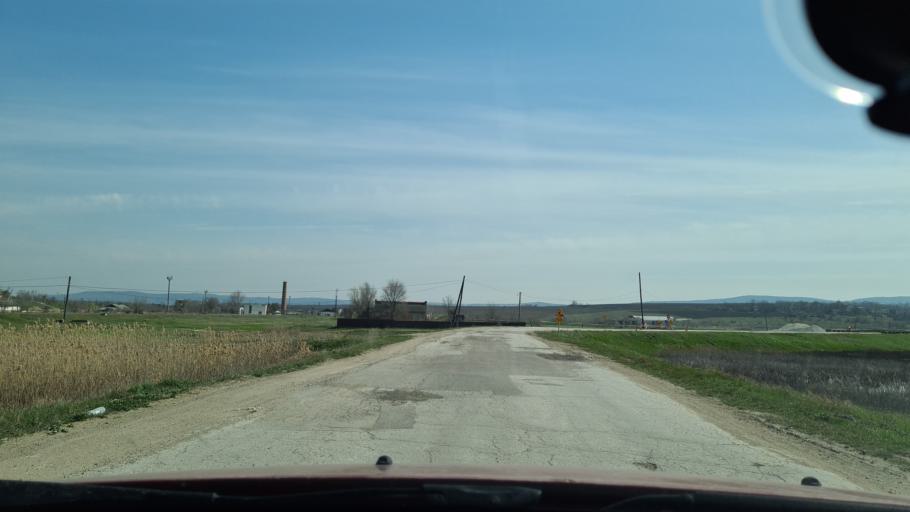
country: MD
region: Ungheni
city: Ungheni
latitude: 47.3207
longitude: 27.8910
